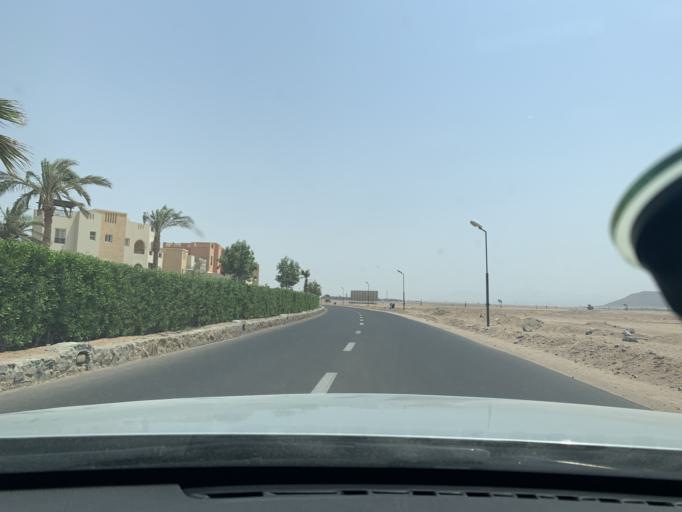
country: EG
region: Red Sea
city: El Gouna
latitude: 27.3798
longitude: 33.6585
